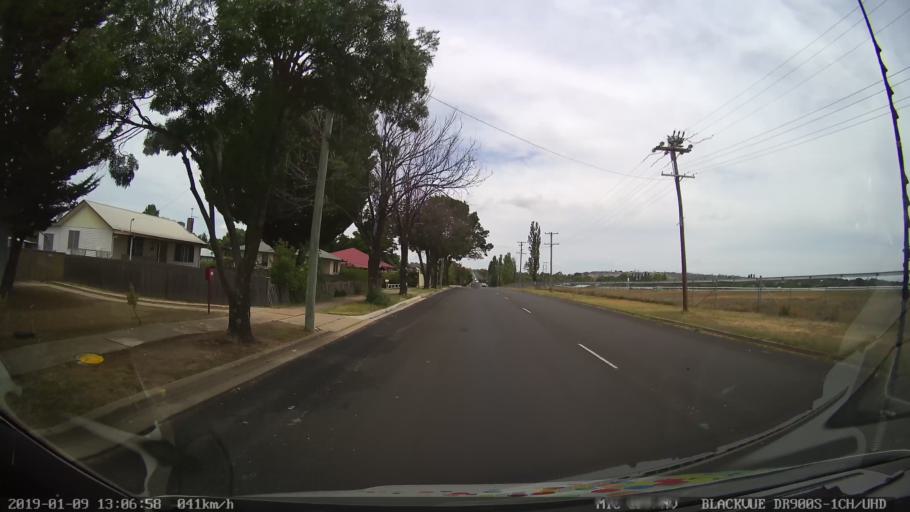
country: AU
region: New South Wales
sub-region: Armidale Dumaresq
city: Armidale
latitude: -30.5164
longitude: 151.6808
